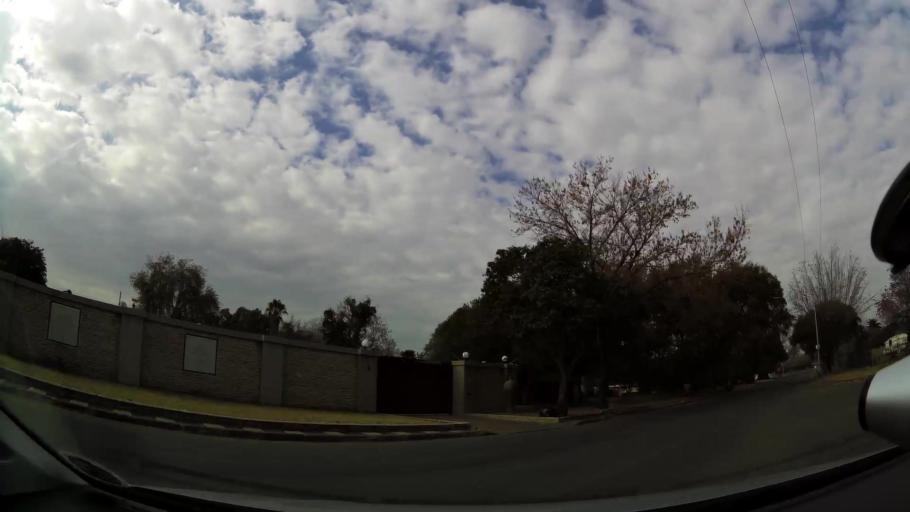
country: ZA
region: Orange Free State
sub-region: Mangaung Metropolitan Municipality
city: Bloemfontein
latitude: -29.0850
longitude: 26.2545
